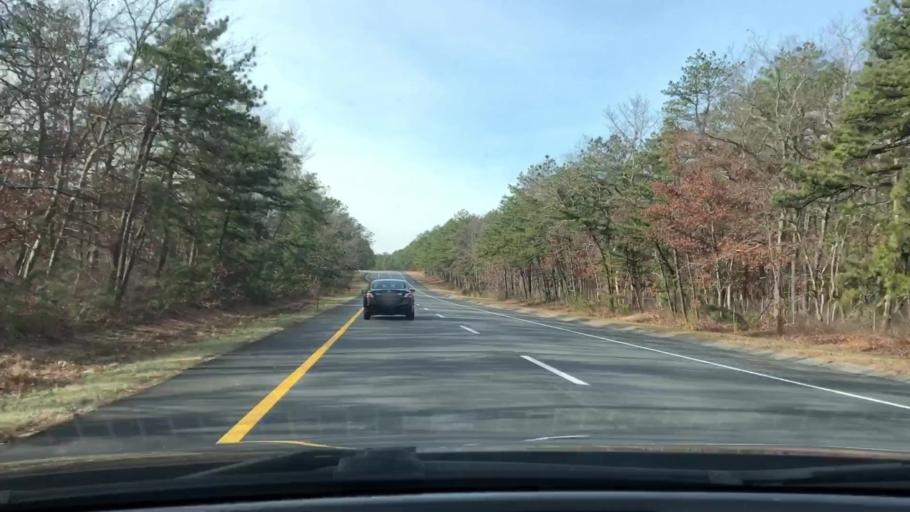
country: US
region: New York
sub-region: Suffolk County
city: Calverton
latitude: 40.9055
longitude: -72.7210
